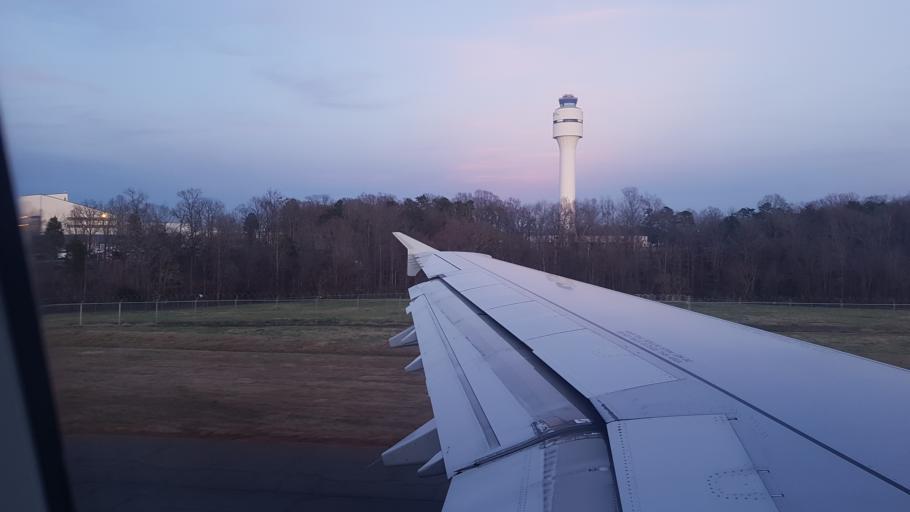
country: US
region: North Carolina
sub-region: Gaston County
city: Belmont
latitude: 35.2036
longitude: -80.9490
